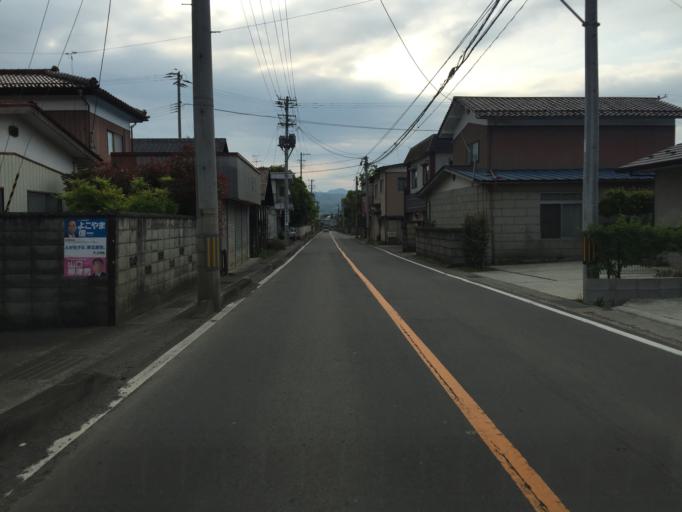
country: JP
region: Fukushima
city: Yanagawamachi-saiwaicho
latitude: 37.8765
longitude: 140.5959
